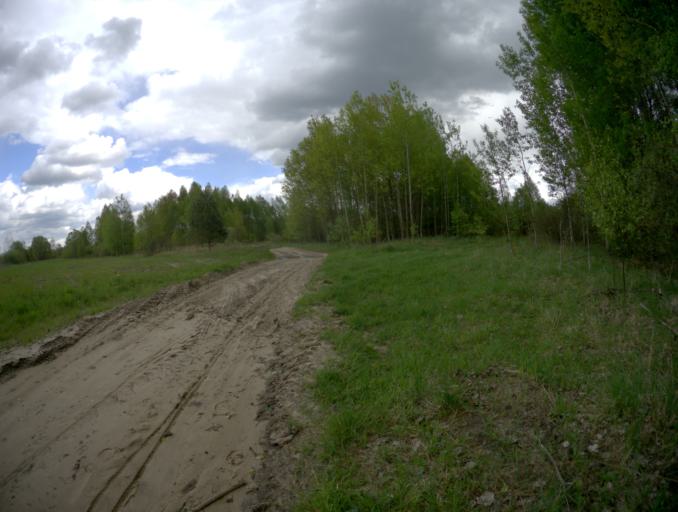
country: RU
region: Moskovskaya
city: Cherusti
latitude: 55.5856
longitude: 40.0426
